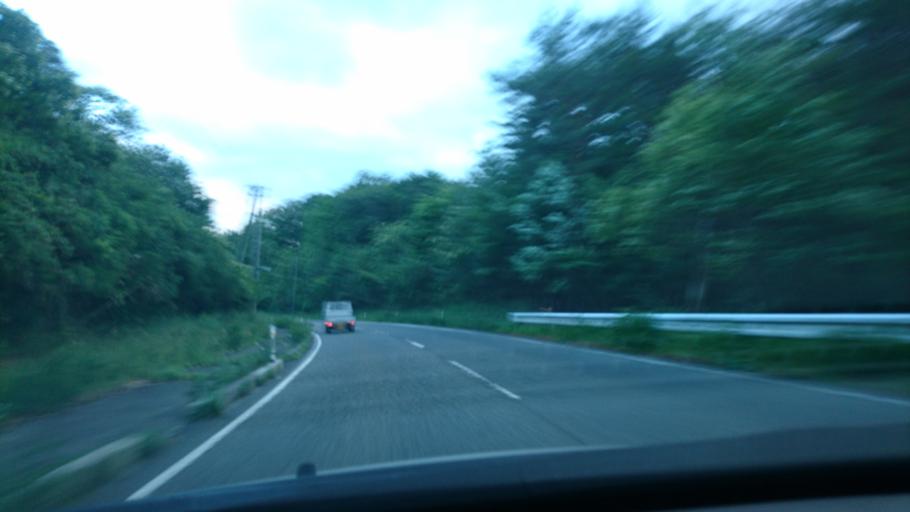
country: JP
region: Iwate
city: Ichinoseki
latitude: 38.7853
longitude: 141.0557
